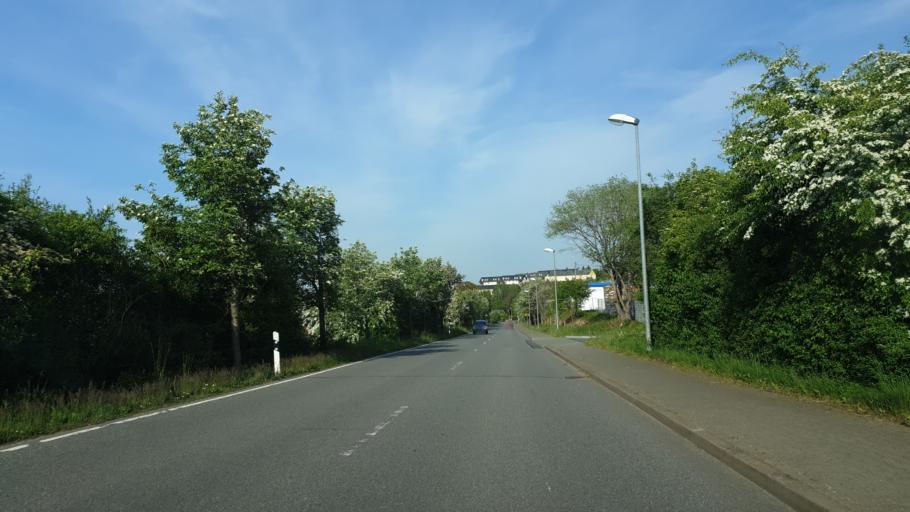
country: DE
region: Saxony
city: Jahnsdorf
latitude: 50.7529
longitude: 12.8534
